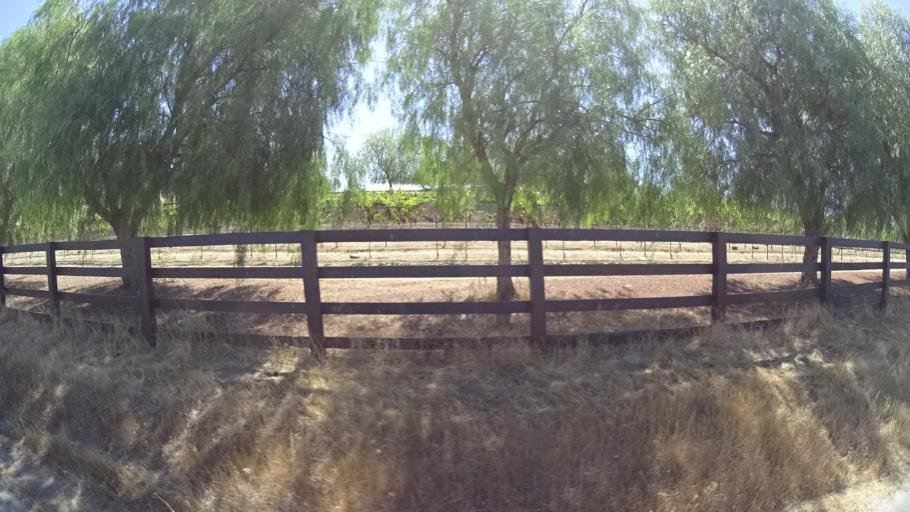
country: US
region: California
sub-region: San Diego County
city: San Diego Country Estates
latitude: 33.0616
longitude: -116.7516
